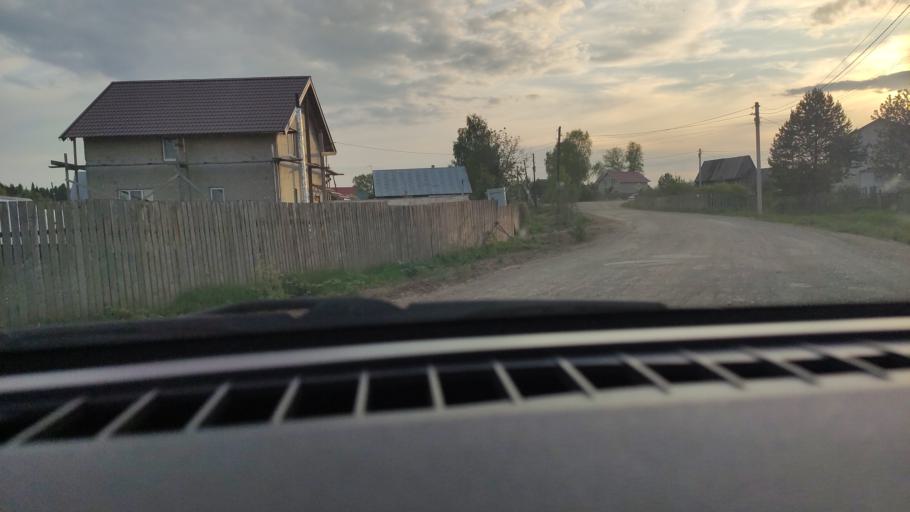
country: RU
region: Perm
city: Overyata
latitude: 58.0789
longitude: 55.9753
